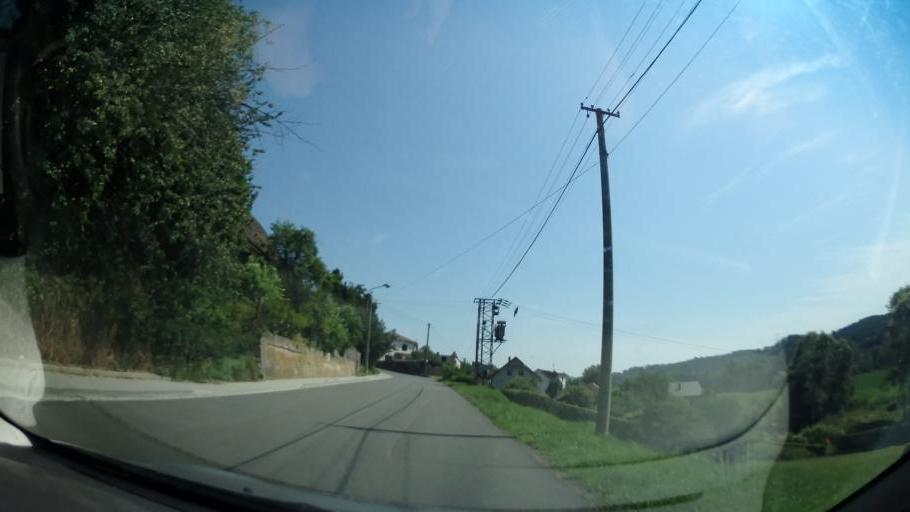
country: CZ
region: Olomoucky
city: Zabreh
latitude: 49.8727
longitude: 16.8476
